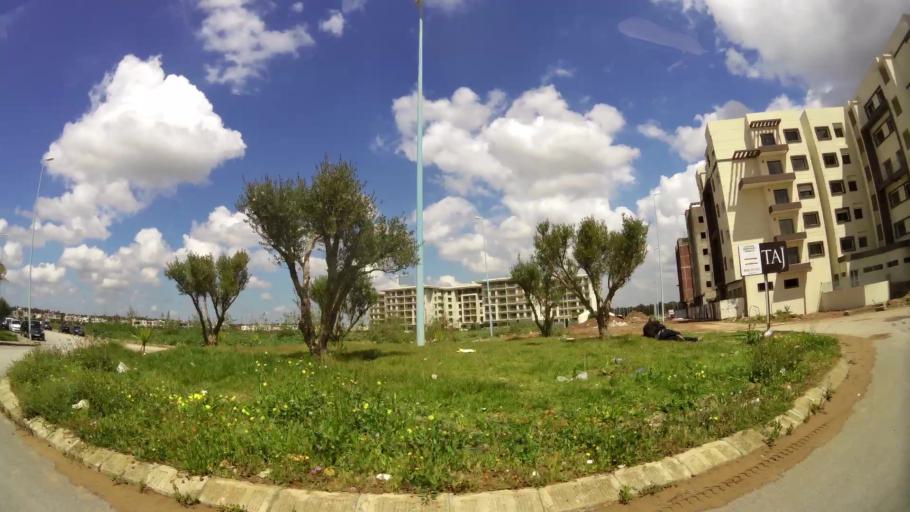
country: MA
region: Chaouia-Ouardigha
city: Nouaseur
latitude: 33.3910
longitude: -7.5612
